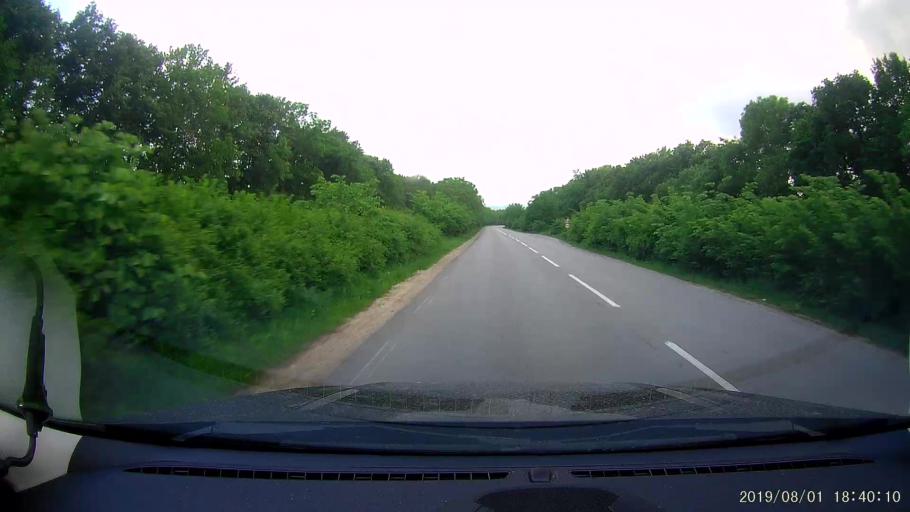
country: BG
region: Shumen
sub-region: Obshtina Khitrino
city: Gara Khitrino
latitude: 43.3722
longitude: 26.9201
